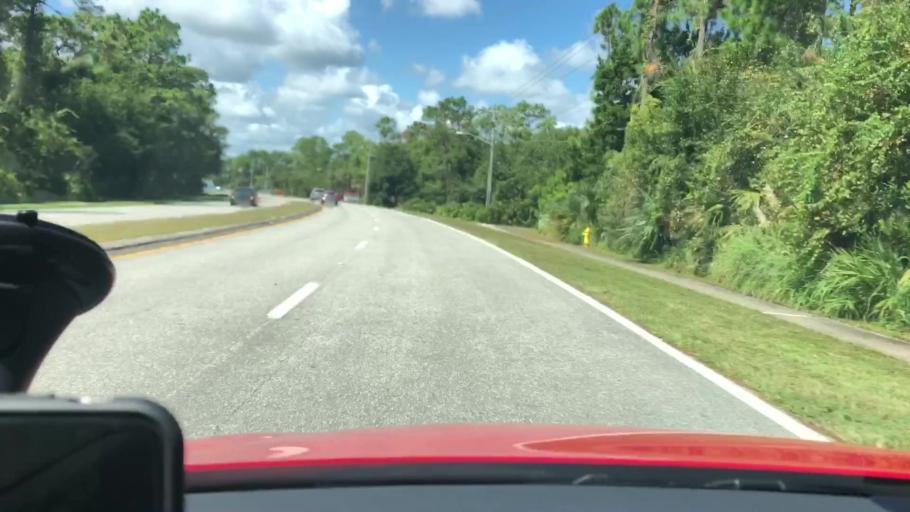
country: US
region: Florida
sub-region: Volusia County
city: Ormond Beach
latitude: 29.2690
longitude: -81.0945
